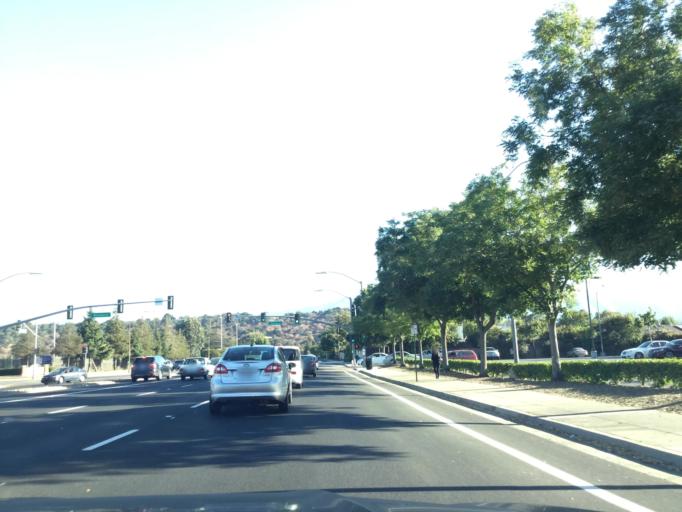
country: US
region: California
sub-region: Santa Clara County
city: Seven Trees
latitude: 37.2487
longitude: -121.8591
